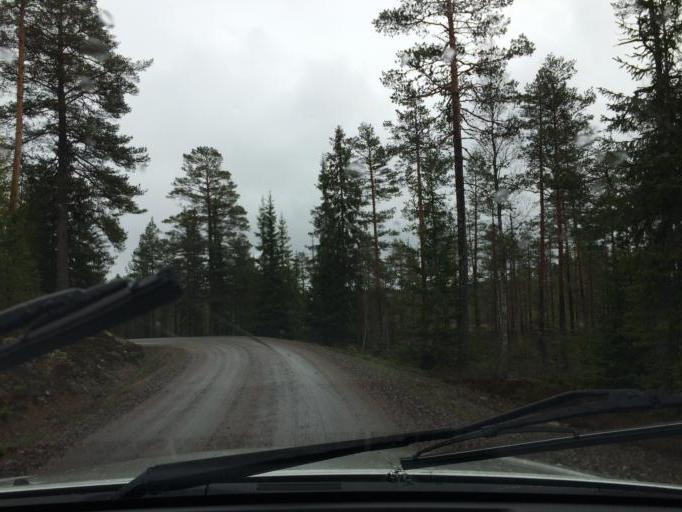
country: SE
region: OErebro
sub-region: Hallefors Kommun
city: Haellefors
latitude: 60.0238
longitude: 14.5607
